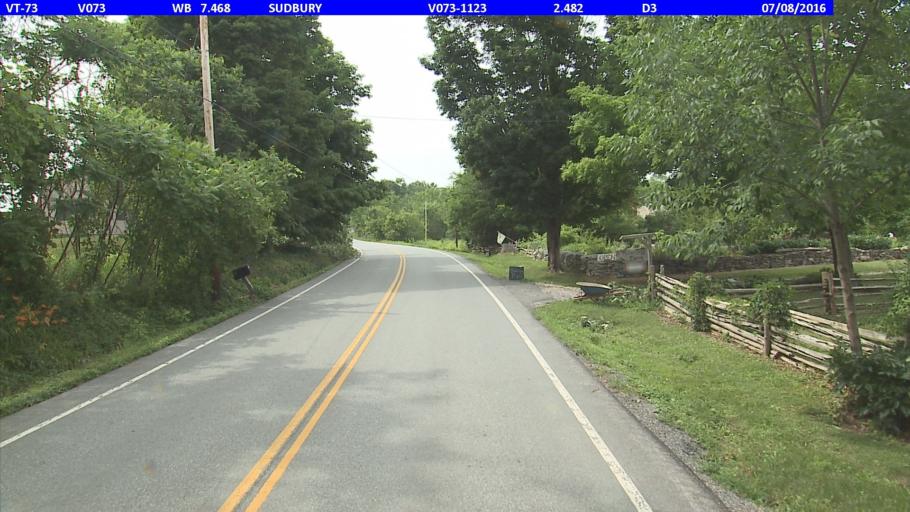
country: US
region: Vermont
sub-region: Rutland County
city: Brandon
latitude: 43.8133
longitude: -73.1579
